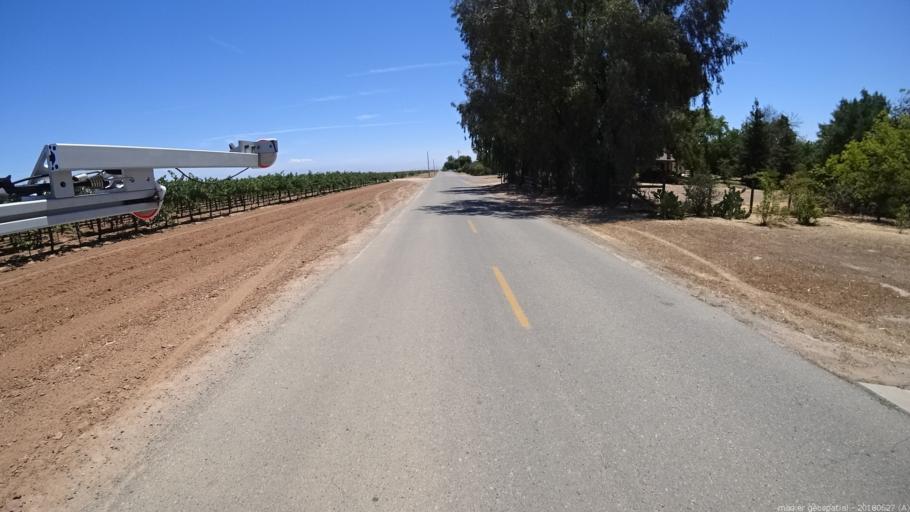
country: US
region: California
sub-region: Madera County
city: Bonadelle Ranchos-Madera Ranchos
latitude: 36.9375
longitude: -119.8770
